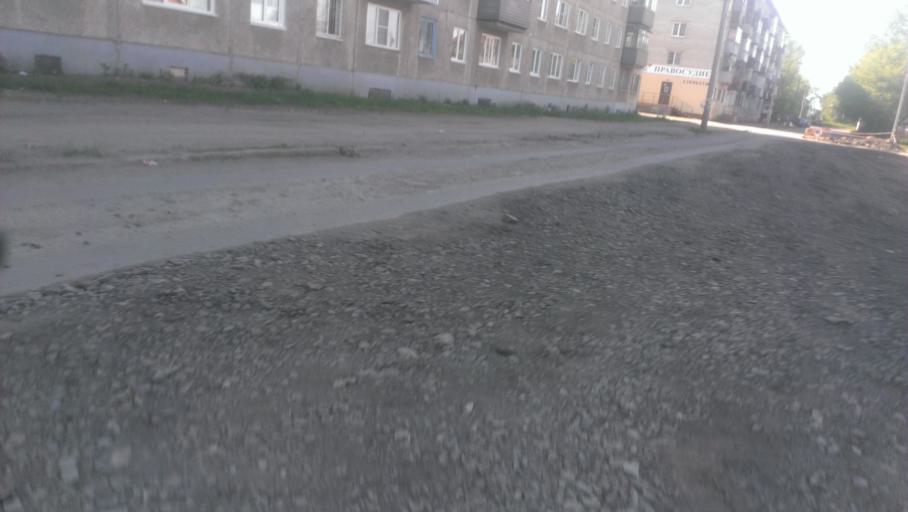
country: RU
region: Altai Krai
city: Novoaltaysk
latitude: 53.3957
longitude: 83.9362
